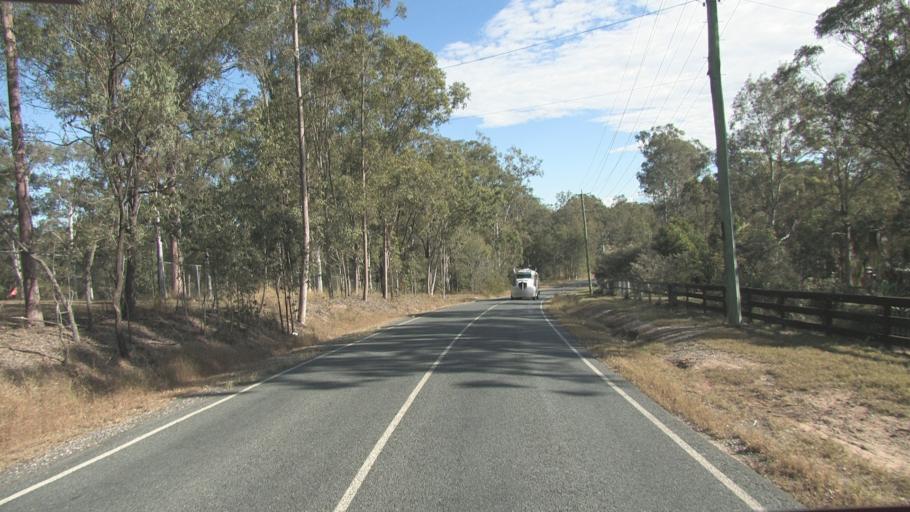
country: AU
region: Queensland
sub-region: Logan
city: Cedar Vale
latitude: -27.8355
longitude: 153.0505
